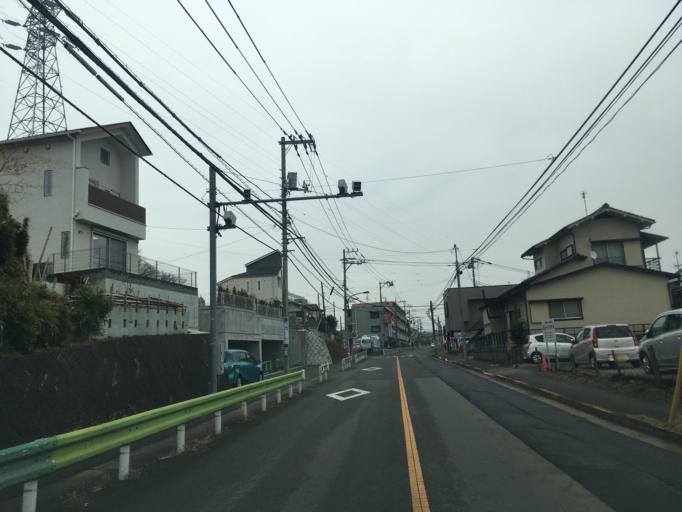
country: JP
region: Tokyo
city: Hino
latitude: 35.6356
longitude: 139.4443
